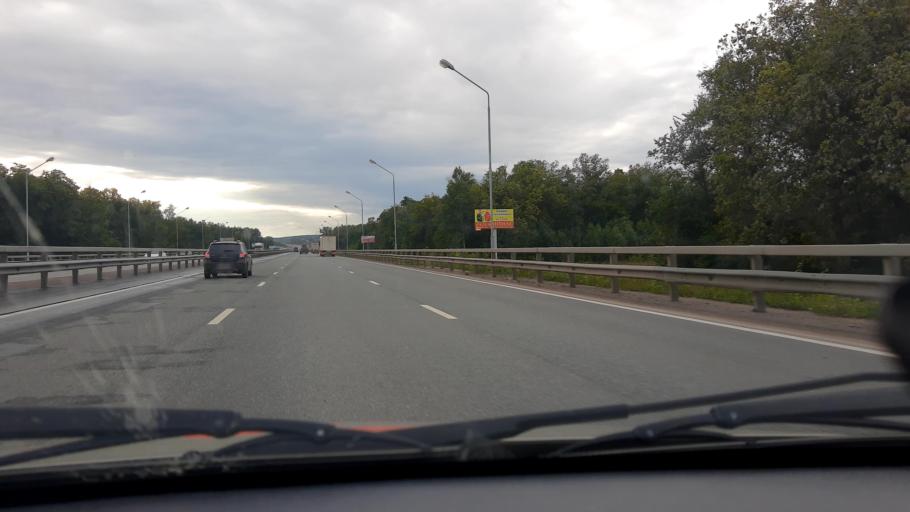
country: RU
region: Bashkortostan
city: Avdon
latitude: 54.6669
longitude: 55.8497
